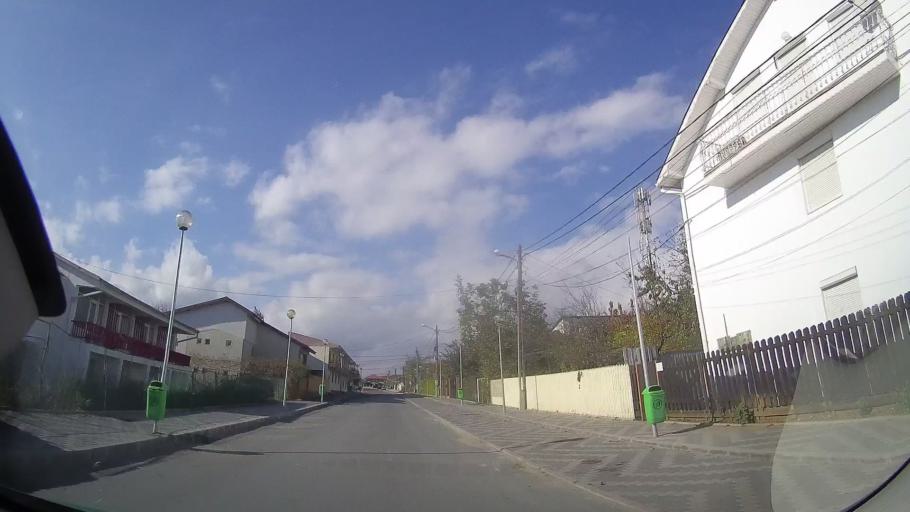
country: RO
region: Constanta
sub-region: Comuna Costinesti
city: Costinesti
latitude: 43.9528
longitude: 28.6380
